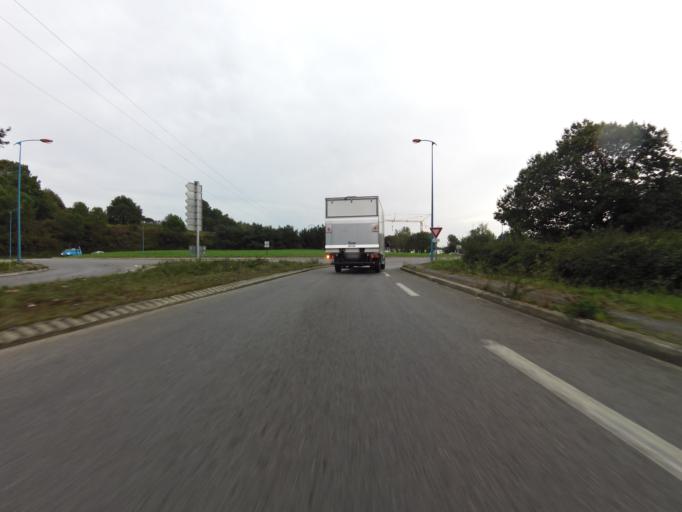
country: FR
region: Brittany
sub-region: Departement du Morbihan
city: Saint-Ave
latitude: 47.6890
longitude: -2.7520
